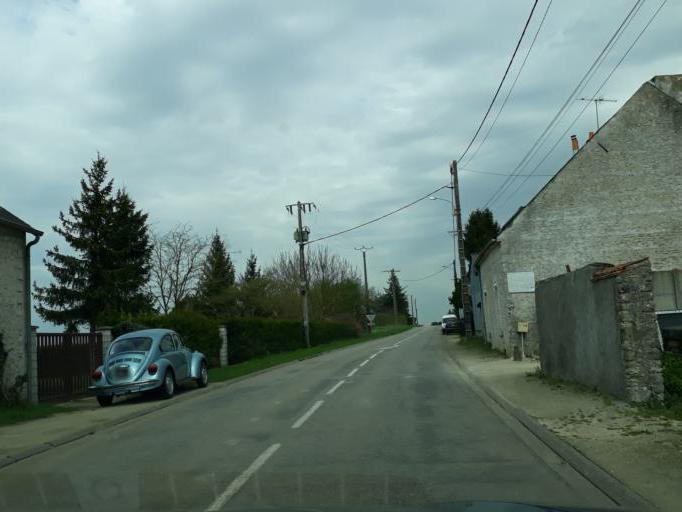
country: FR
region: Centre
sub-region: Departement du Loiret
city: Epieds-en-Beauce
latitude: 47.9295
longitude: 1.5777
